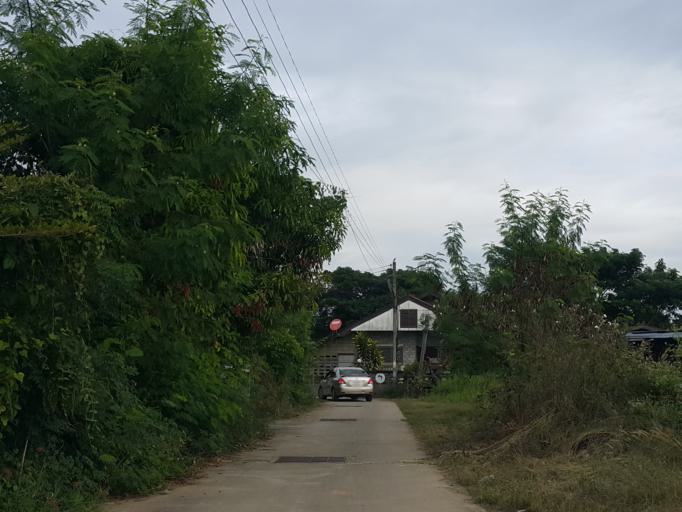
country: TH
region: Lampang
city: Lampang
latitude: 18.3006
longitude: 99.5028
